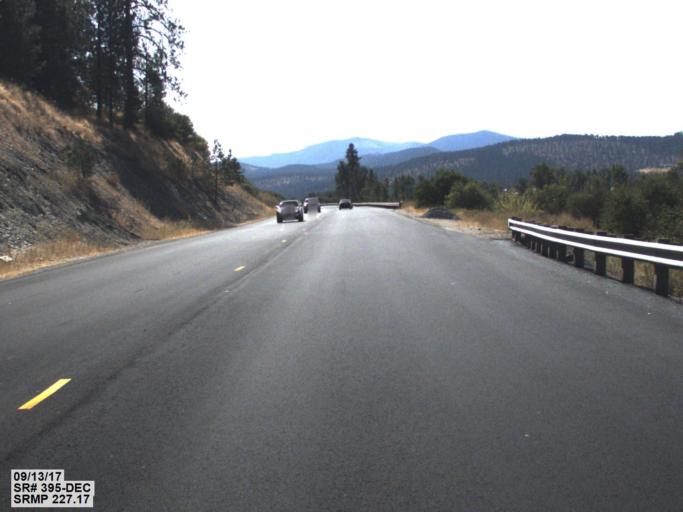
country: US
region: Washington
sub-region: Stevens County
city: Colville
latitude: 48.5114
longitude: -117.9008
